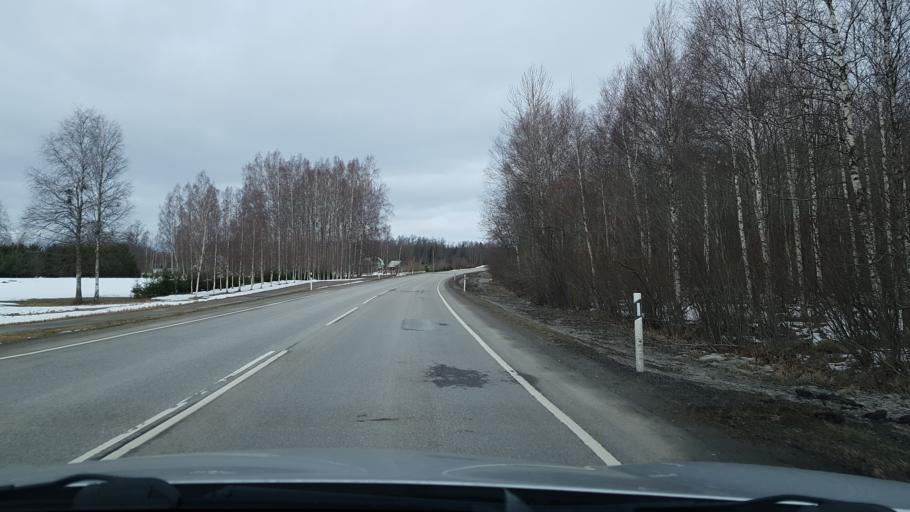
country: EE
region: Jogevamaa
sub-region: Tabivere vald
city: Tabivere
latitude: 58.5603
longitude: 26.5912
